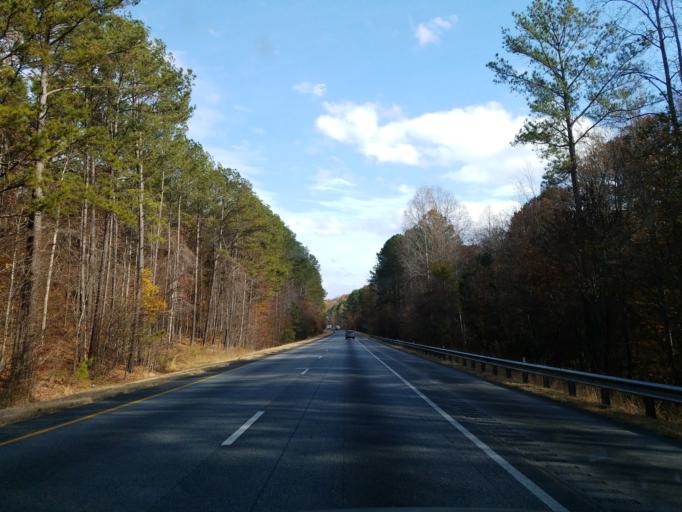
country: US
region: Alabama
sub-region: Cleburne County
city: Heflin
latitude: 33.6190
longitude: -85.6243
